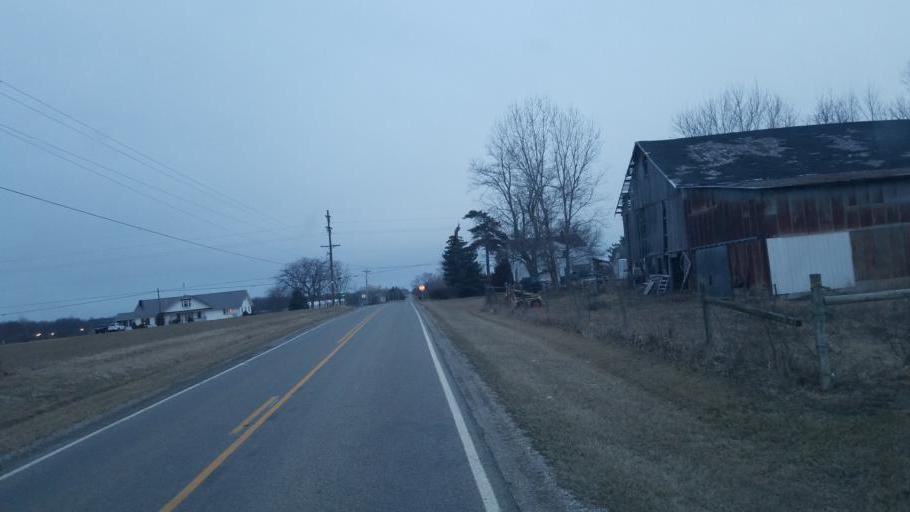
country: US
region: Ohio
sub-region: Defiance County
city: Hicksville
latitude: 41.3249
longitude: -84.7652
